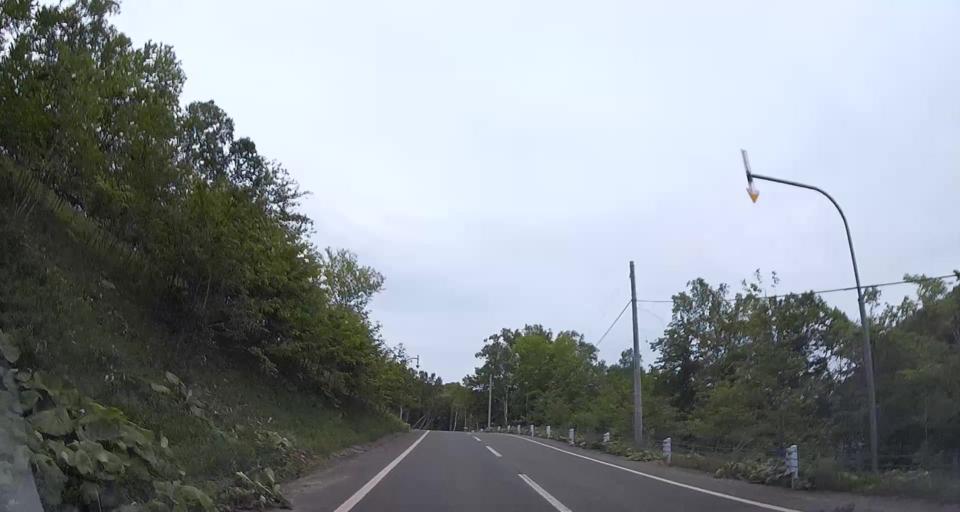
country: JP
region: Hokkaido
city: Chitose
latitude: 42.7922
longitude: 142.0407
